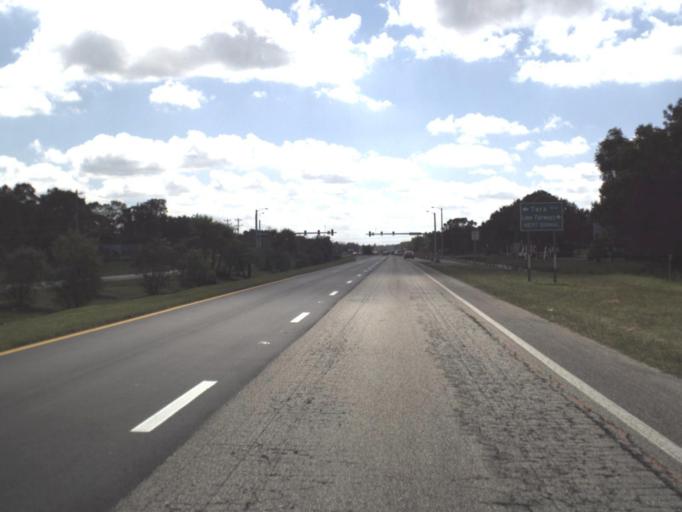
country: US
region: Florida
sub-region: Lee County
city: Suncoast Estates
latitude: 26.7482
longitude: -81.9194
